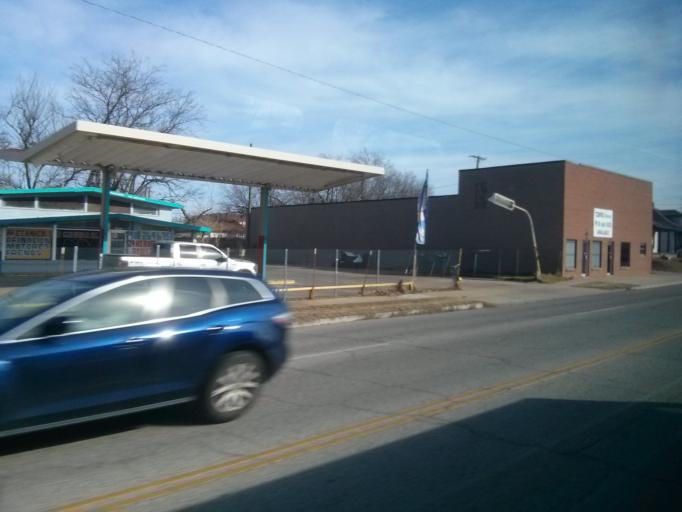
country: US
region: Oklahoma
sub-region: Tulsa County
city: Tulsa
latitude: 36.1566
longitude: -95.9634
